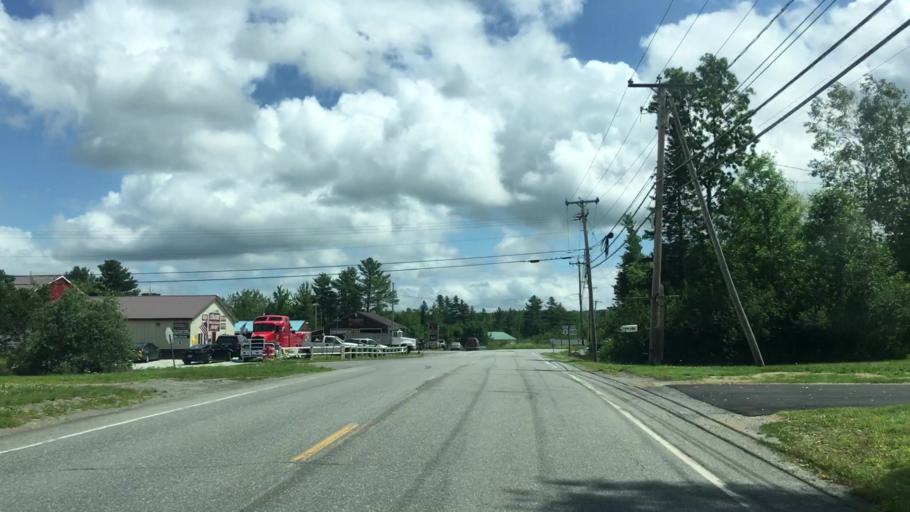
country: US
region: Maine
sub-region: Penobscot County
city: Hermon
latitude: 44.8088
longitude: -68.9809
